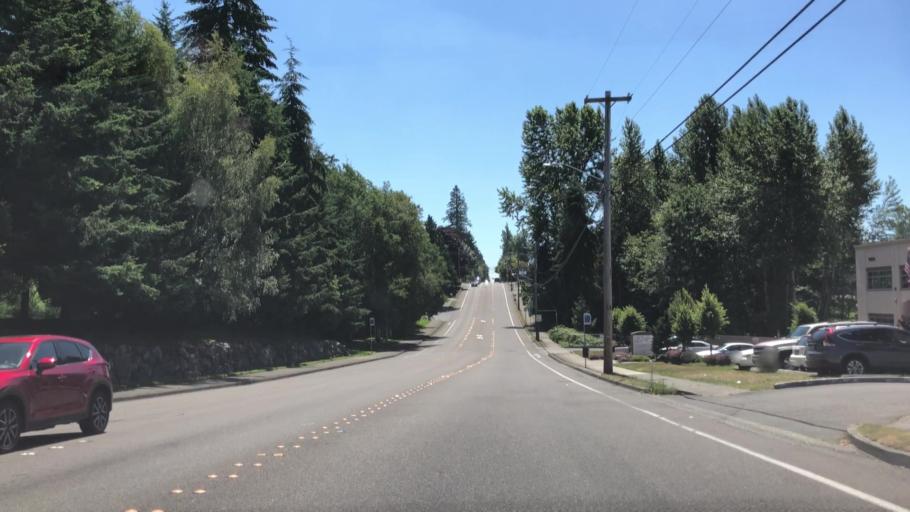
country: US
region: Washington
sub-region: Snohomish County
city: Alderwood Manor
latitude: 47.8464
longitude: -122.2925
